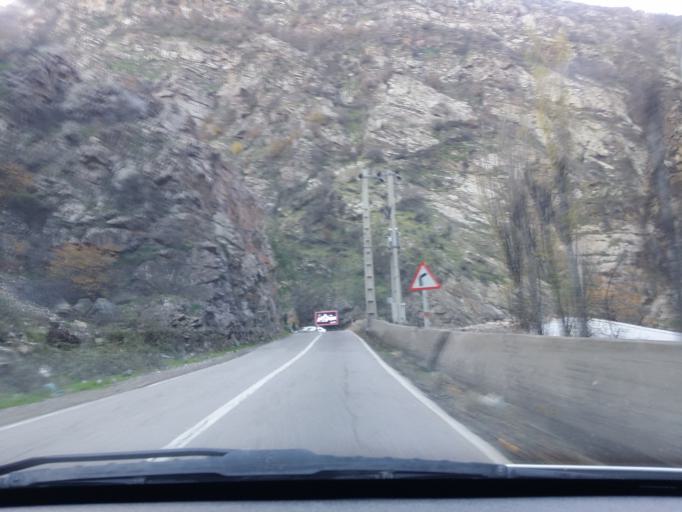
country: IR
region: Mazandaran
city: Chalus
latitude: 36.3015
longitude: 51.2478
